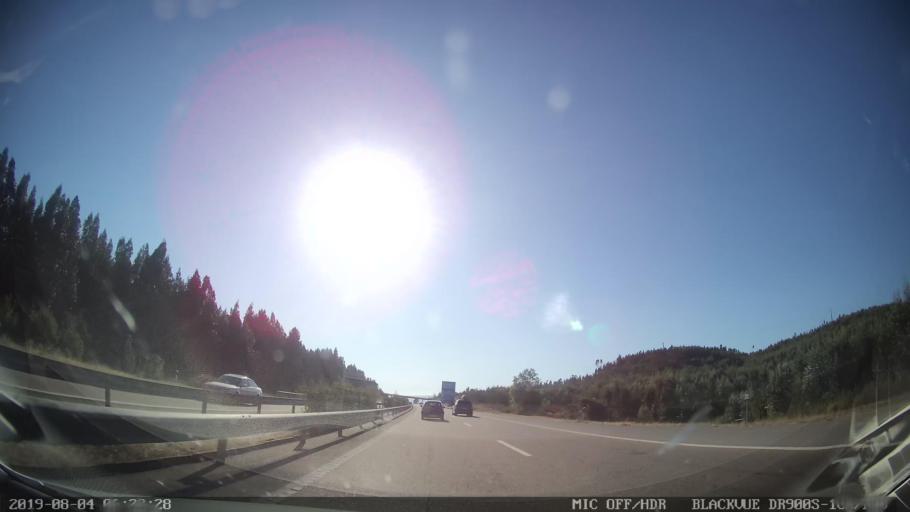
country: PT
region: Santarem
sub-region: Chamusca
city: Vila Nova da Barquinha
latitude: 39.4893
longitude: -8.4275
